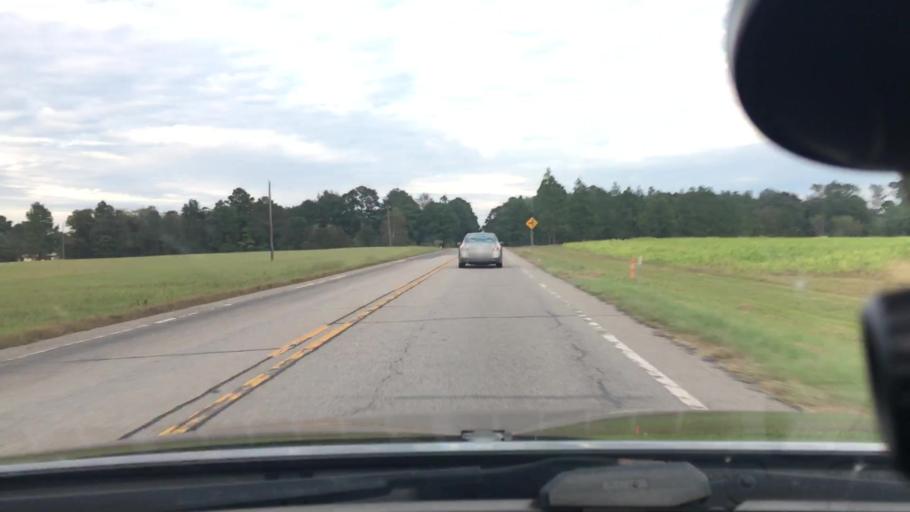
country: US
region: North Carolina
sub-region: Moore County
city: Carthage
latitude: 35.3714
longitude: -79.3037
